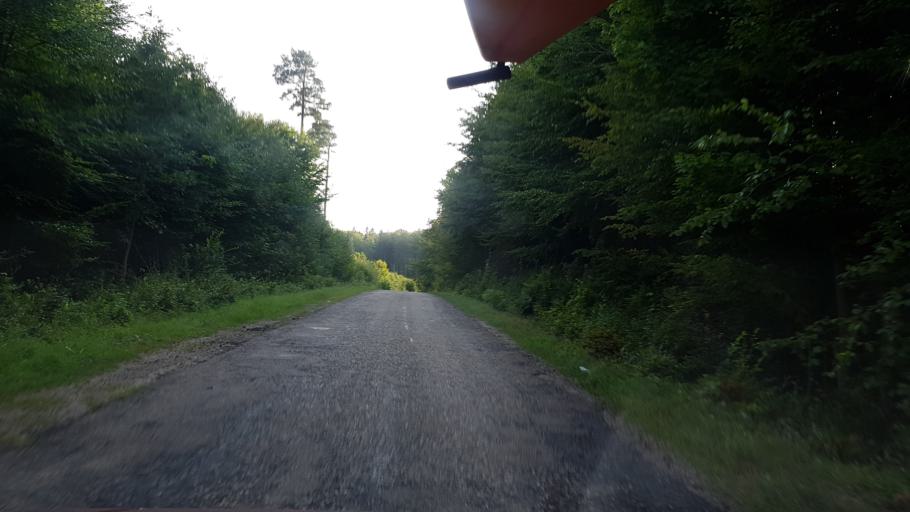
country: PL
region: Pomeranian Voivodeship
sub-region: Powiat bytowski
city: Miastko
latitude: 53.9853
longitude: 16.8988
